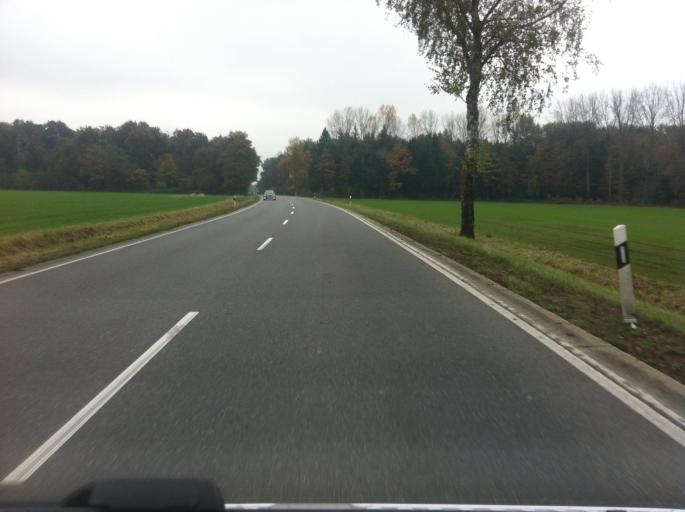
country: DE
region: North Rhine-Westphalia
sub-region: Regierungsbezirk Munster
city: Sudlohn
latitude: 51.9765
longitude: 6.8367
